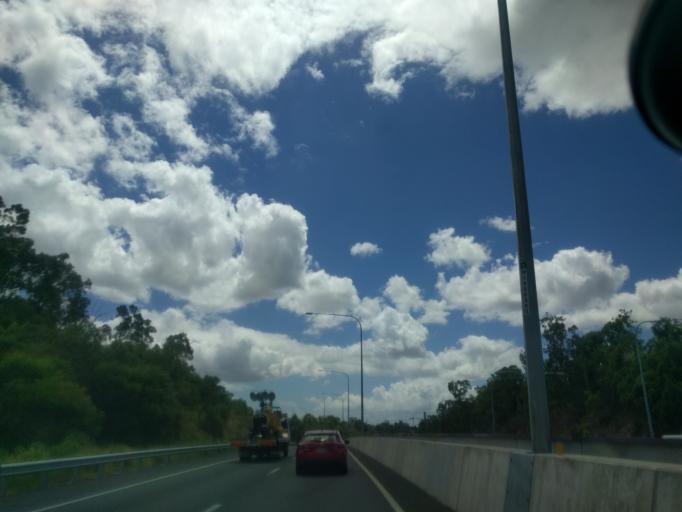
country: AU
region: Queensland
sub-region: Brisbane
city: Taringa
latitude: -27.4797
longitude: 152.9751
